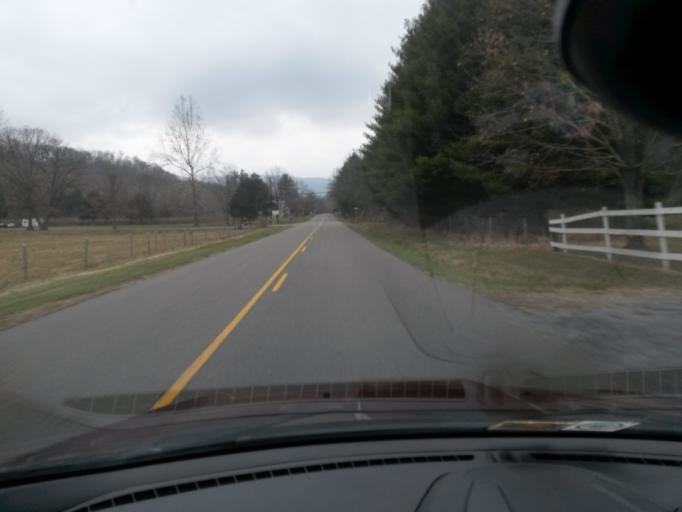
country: US
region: Virginia
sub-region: City of Lexington
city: Lexington
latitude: 37.8586
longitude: -79.5036
